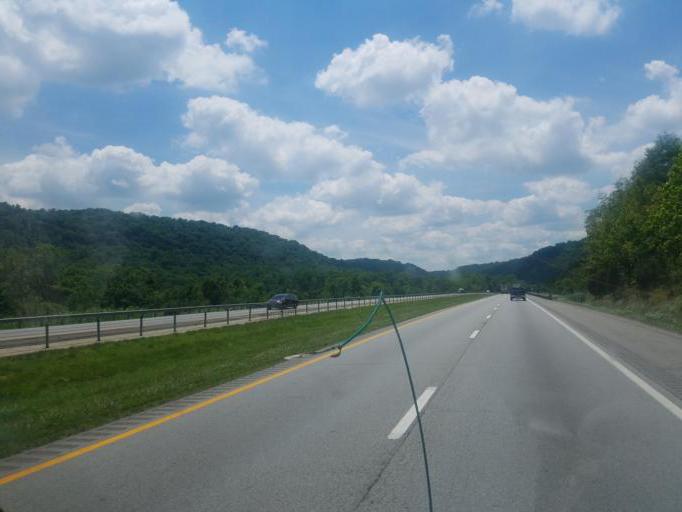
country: US
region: Kentucky
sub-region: Carroll County
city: Carrollton
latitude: 38.6161
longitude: -85.1617
